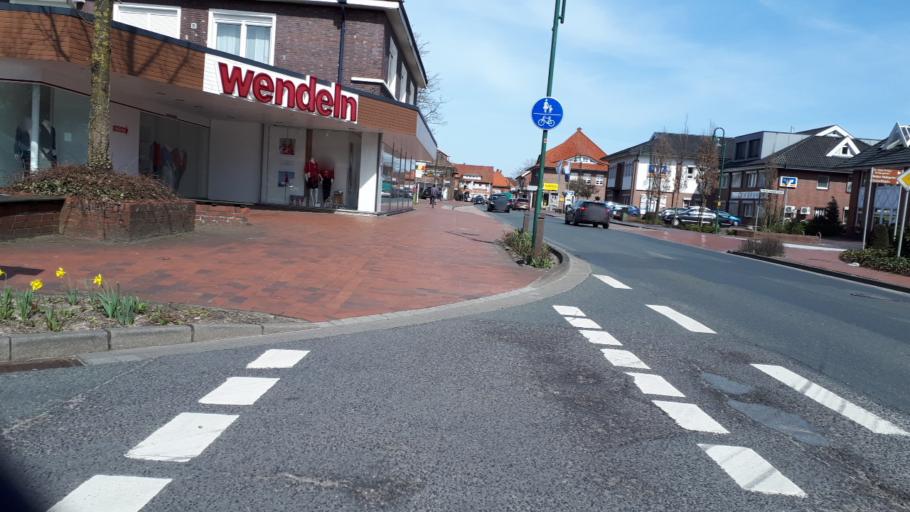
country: DE
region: Lower Saxony
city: Garrel
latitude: 52.9550
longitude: 8.0241
